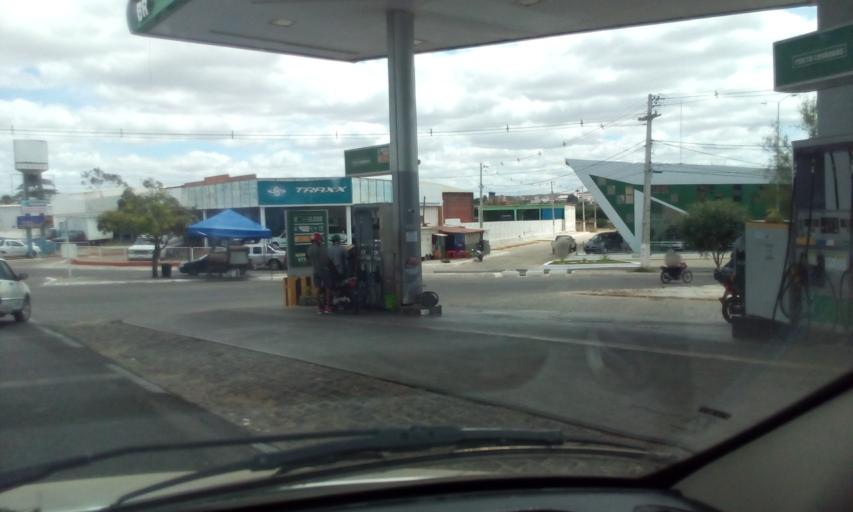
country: BR
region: Rio Grande do Norte
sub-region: Currais Novos
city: Currais Novos
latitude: -6.2585
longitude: -36.5133
